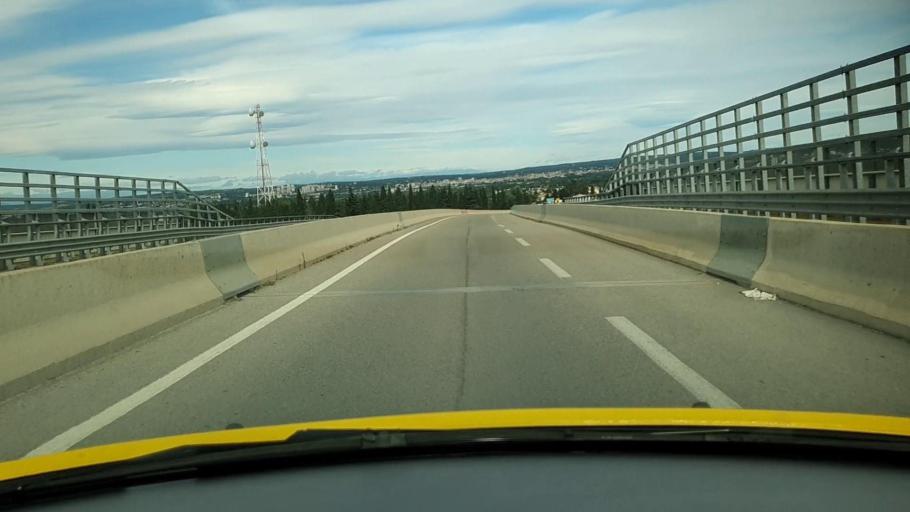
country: FR
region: Languedoc-Roussillon
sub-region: Departement du Gard
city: Caissargues
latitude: 43.7797
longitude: 4.3949
